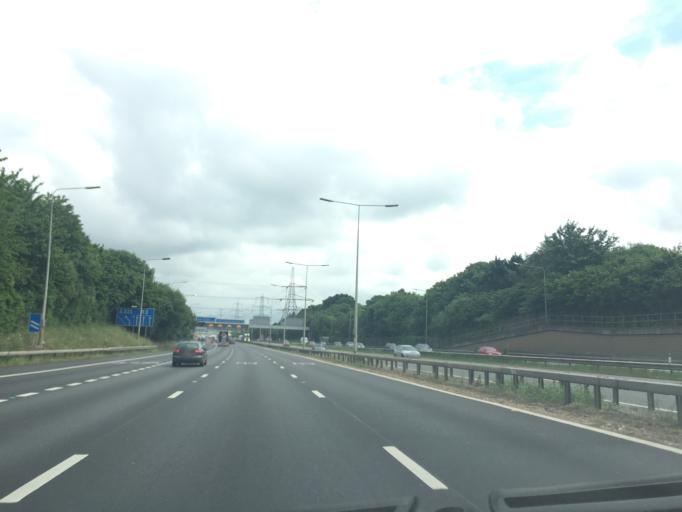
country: GB
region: England
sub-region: Hampshire
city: Eastleigh
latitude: 50.9664
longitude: -1.3822
